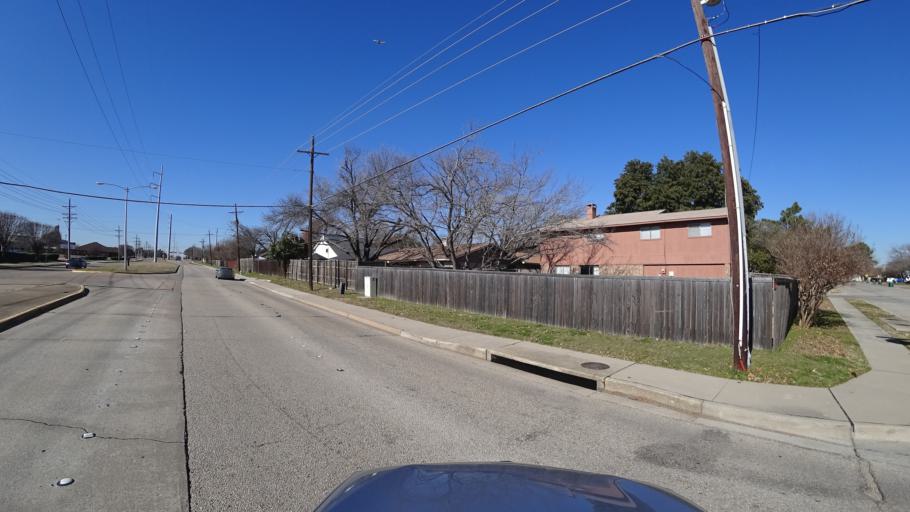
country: US
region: Texas
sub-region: Denton County
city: Lewisville
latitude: 33.0276
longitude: -97.0072
